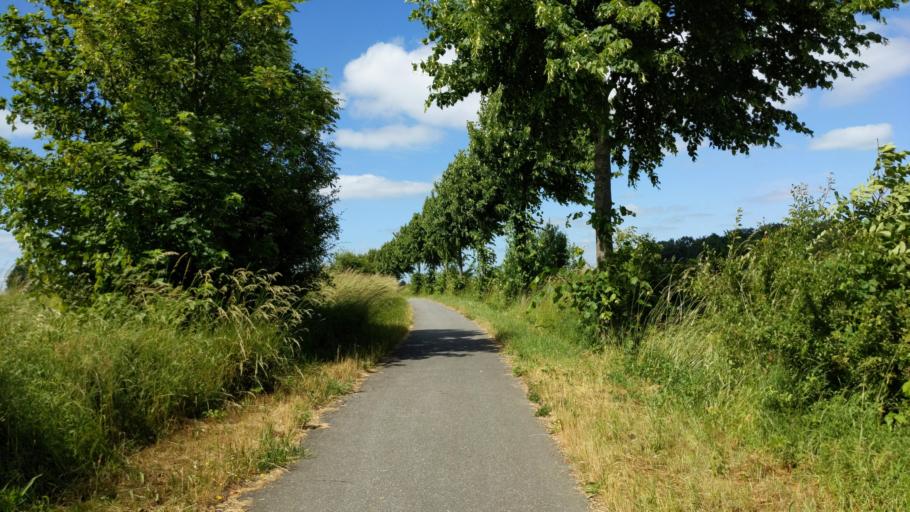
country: DE
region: Schleswig-Holstein
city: Scharbeutz
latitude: 54.0136
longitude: 10.7410
